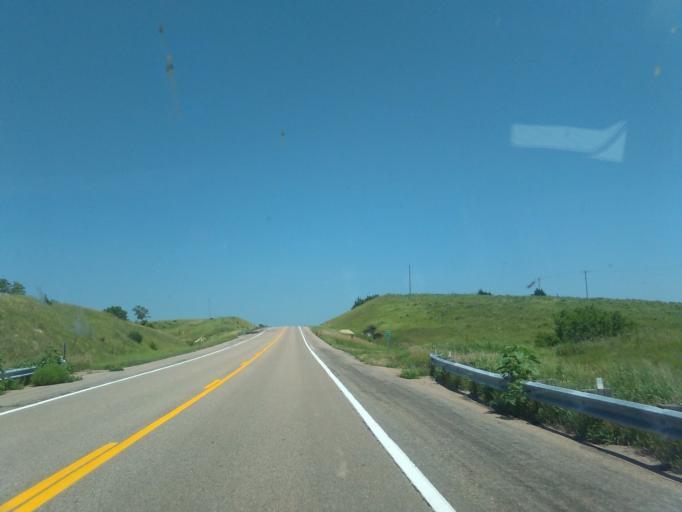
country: US
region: Nebraska
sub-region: Frontier County
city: Stockville
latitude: 40.5860
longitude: -100.6295
